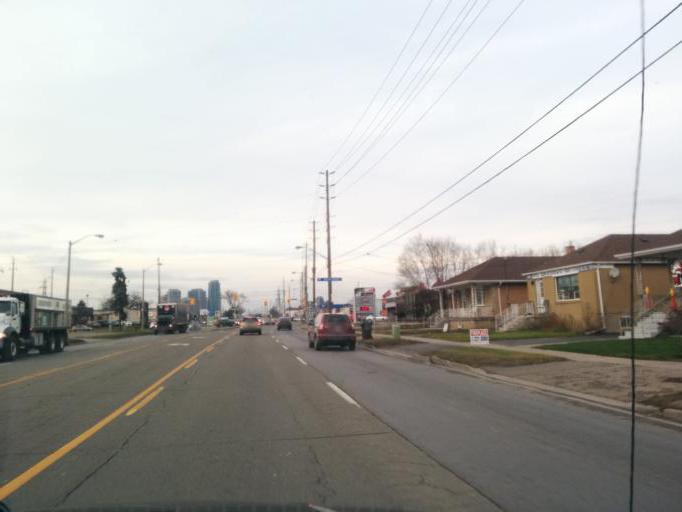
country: CA
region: Ontario
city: Etobicoke
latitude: 43.6241
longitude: -79.5281
